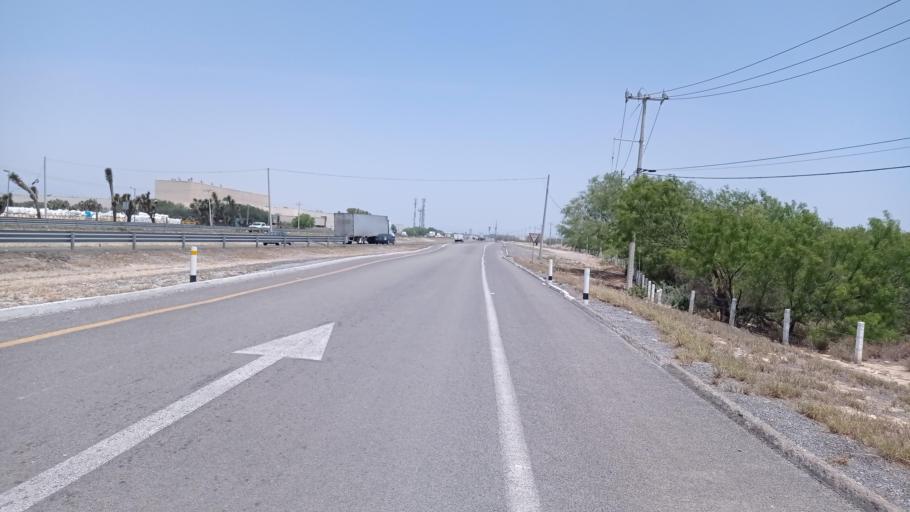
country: MX
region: Nuevo Leon
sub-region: Apodaca
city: Entronque Laredo-Salinas Victoria
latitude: 25.8869
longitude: -100.2206
